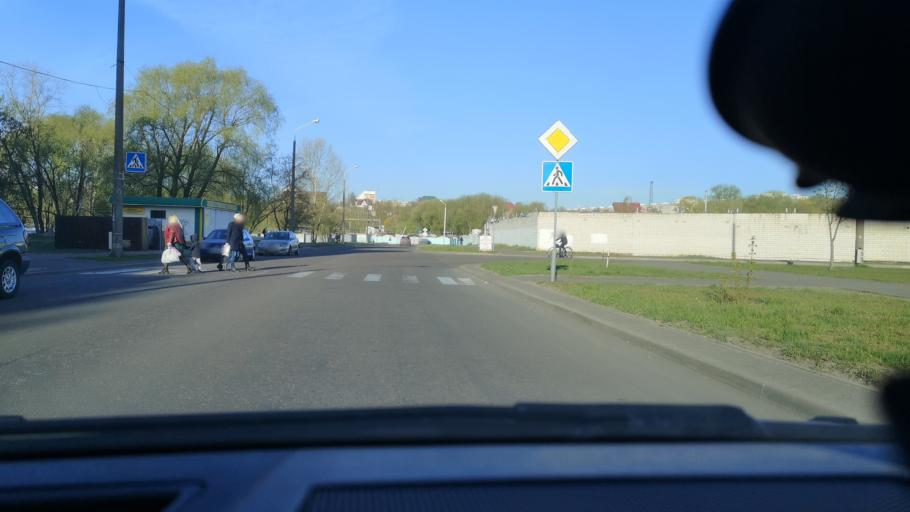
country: BY
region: Gomel
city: Gomel
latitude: 52.4502
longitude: 31.0157
